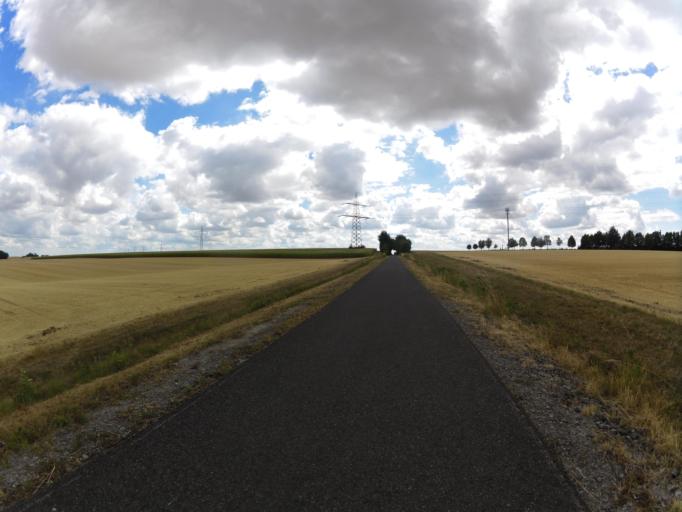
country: DE
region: Bavaria
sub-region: Regierungsbezirk Unterfranken
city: Sonderhofen
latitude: 49.5869
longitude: 10.0082
